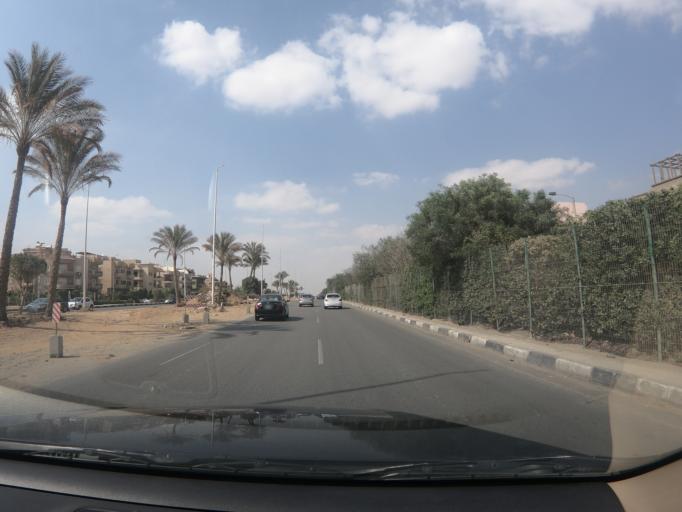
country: EG
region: Muhafazat al Qalyubiyah
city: Al Khankah
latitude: 30.0607
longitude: 31.4751
